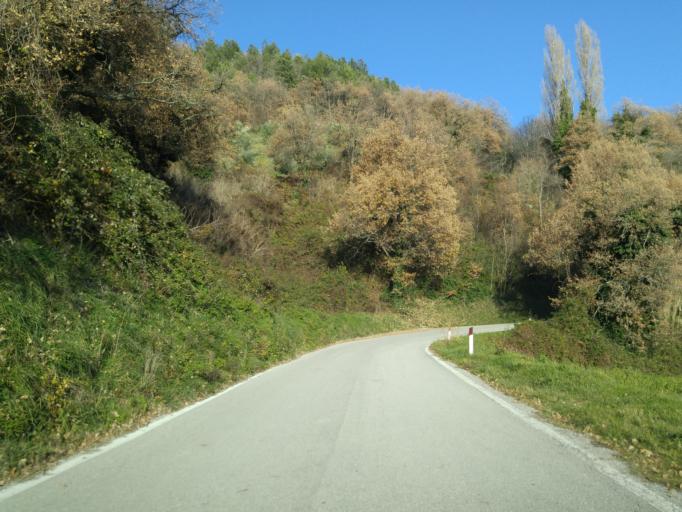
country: IT
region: The Marches
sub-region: Provincia di Pesaro e Urbino
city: Isola del Piano
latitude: 43.7695
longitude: 12.8090
